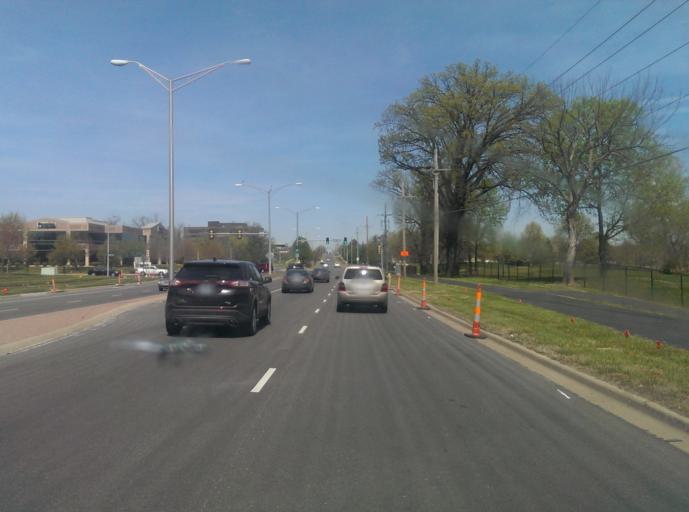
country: US
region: Kansas
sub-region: Johnson County
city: Lenexa
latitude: 38.8891
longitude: -94.6678
